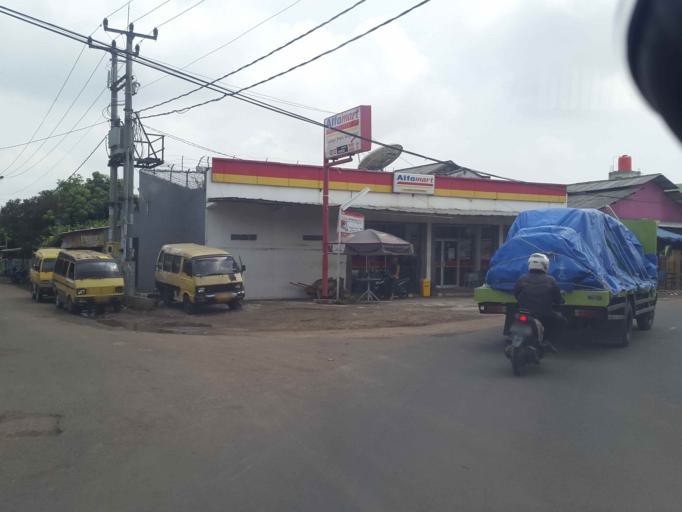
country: ID
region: West Java
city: Rengasdengklok
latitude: -6.2920
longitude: 107.3468
